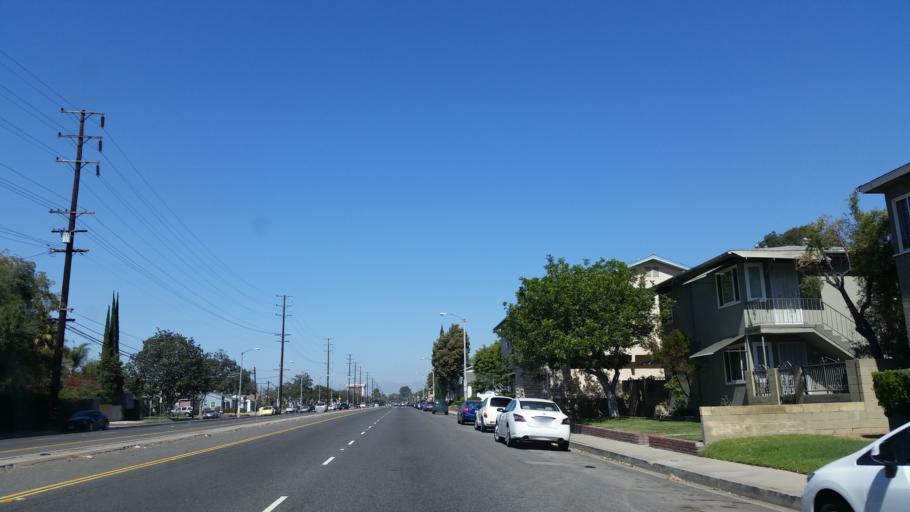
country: US
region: California
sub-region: Los Angeles County
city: Lakewood
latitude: 33.8371
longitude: -118.1425
